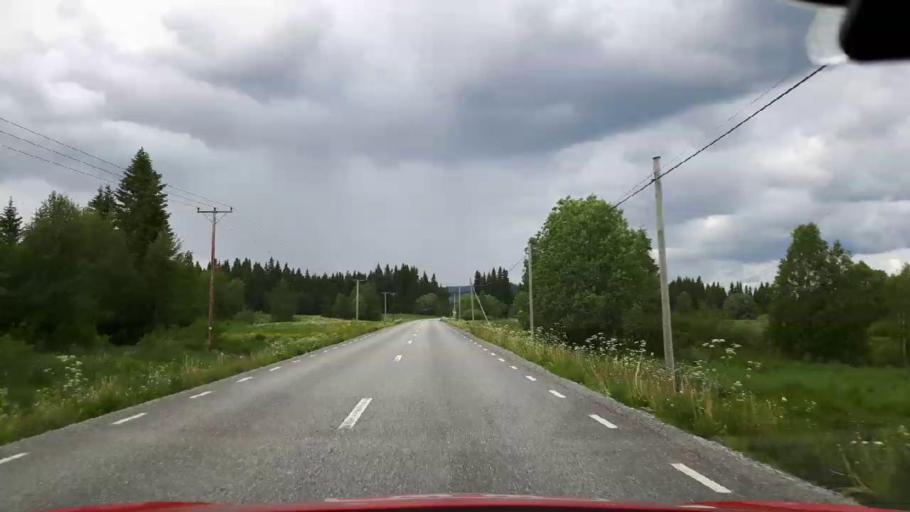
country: SE
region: Jaemtland
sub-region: Krokoms Kommun
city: Krokom
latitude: 63.6753
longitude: 14.3429
